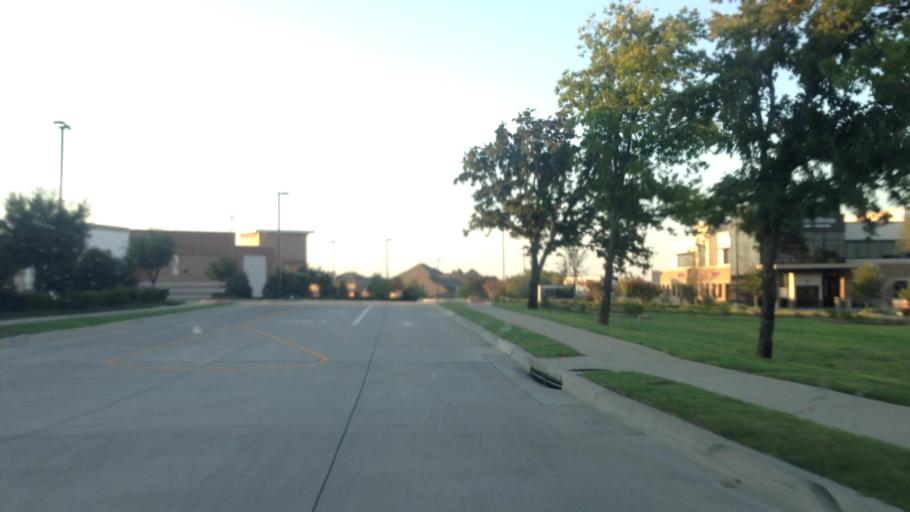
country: US
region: Texas
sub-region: Tarrant County
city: Southlake
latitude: 32.9404
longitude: -97.1369
